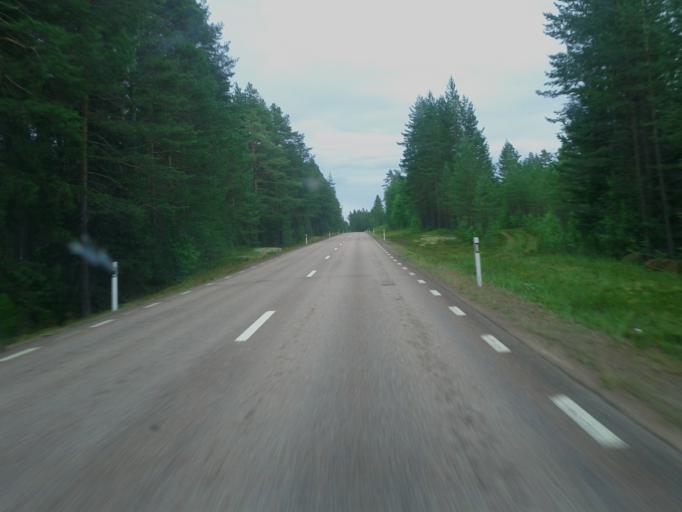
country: SE
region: Dalarna
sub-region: Mora Kommun
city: Mora
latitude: 61.0717
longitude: 14.3708
